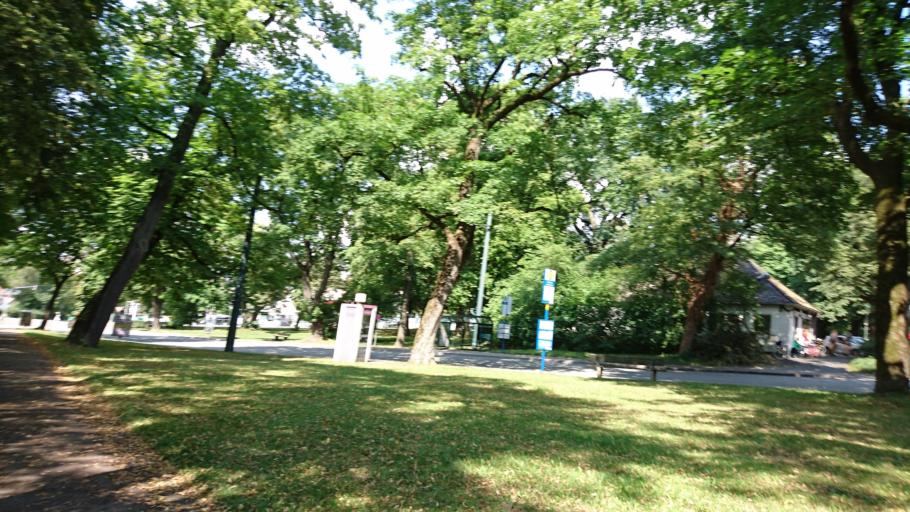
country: DE
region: Bavaria
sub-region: Swabia
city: Augsburg
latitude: 48.3767
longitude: 10.8882
